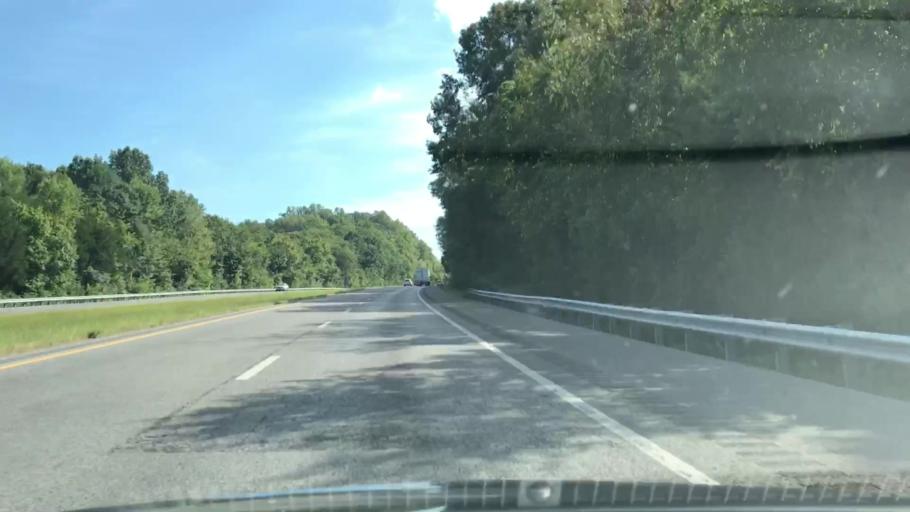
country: US
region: Alabama
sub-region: Limestone County
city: Ardmore
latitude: 35.1230
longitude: -86.8777
